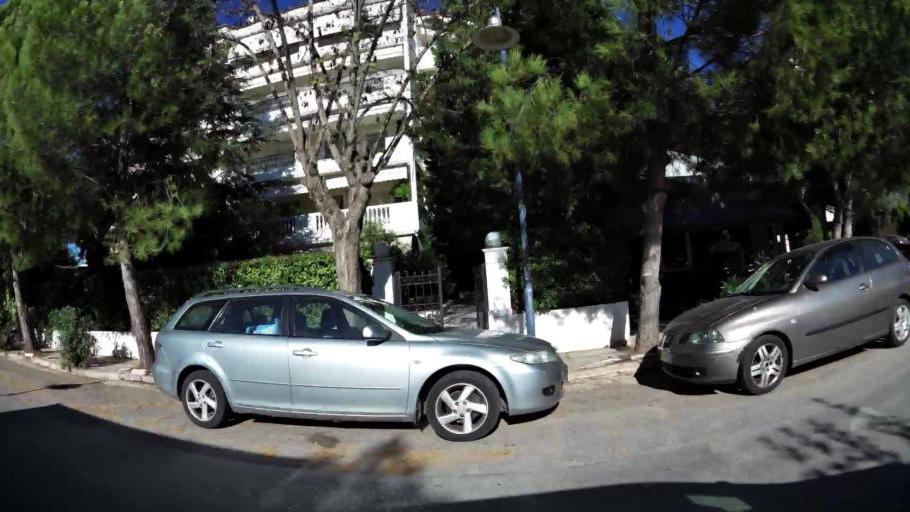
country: GR
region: Attica
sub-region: Nomarchia Athinas
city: Vrilissia
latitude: 38.0343
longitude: 23.8333
